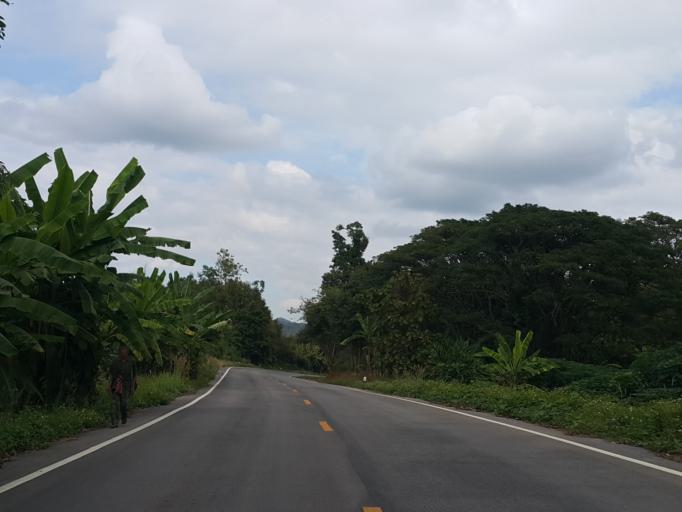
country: TH
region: Lampang
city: Chae Hom
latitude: 18.6226
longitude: 99.4849
